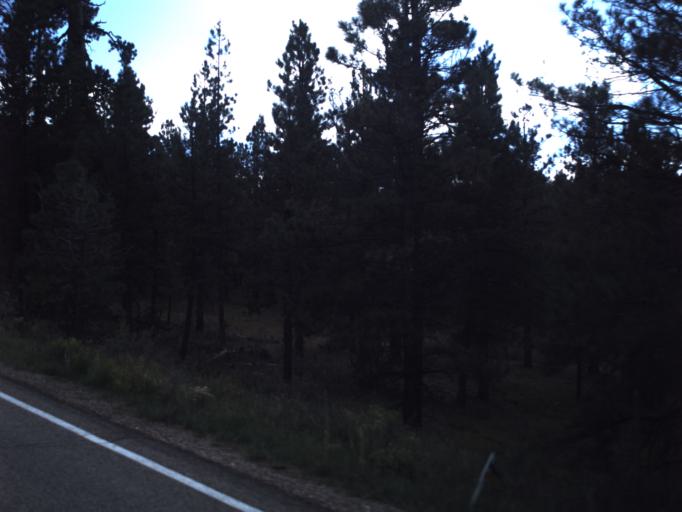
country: US
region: Utah
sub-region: Garfield County
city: Panguitch
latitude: 37.5005
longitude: -112.6226
